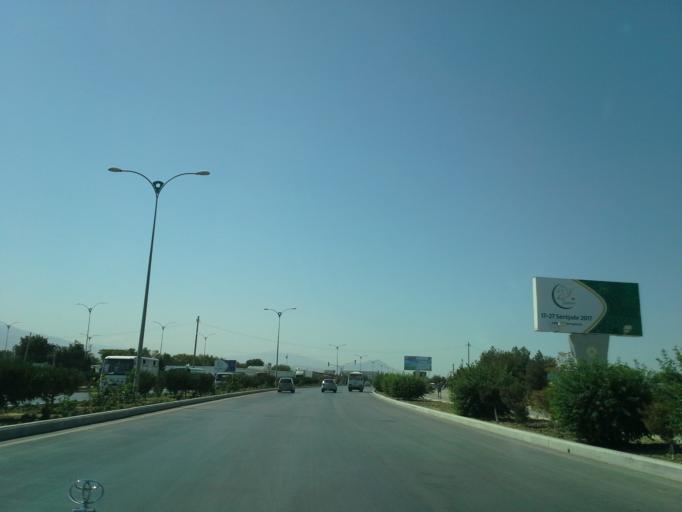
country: TM
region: Ahal
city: Annau
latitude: 37.9077
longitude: 58.5116
